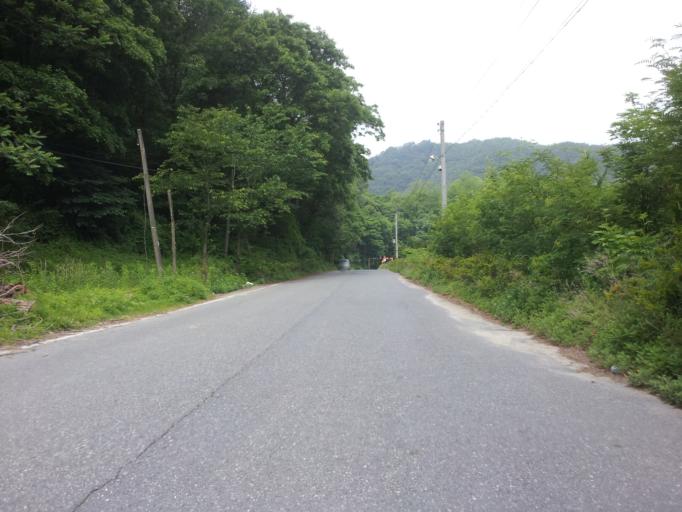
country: KR
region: Daejeon
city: Daejeon
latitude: 36.3347
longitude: 127.4916
